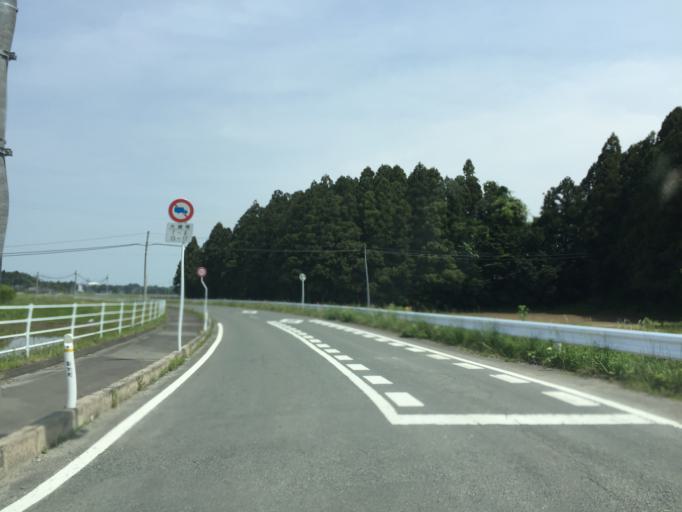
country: JP
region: Miyagi
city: Marumori
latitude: 37.8477
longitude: 140.8956
